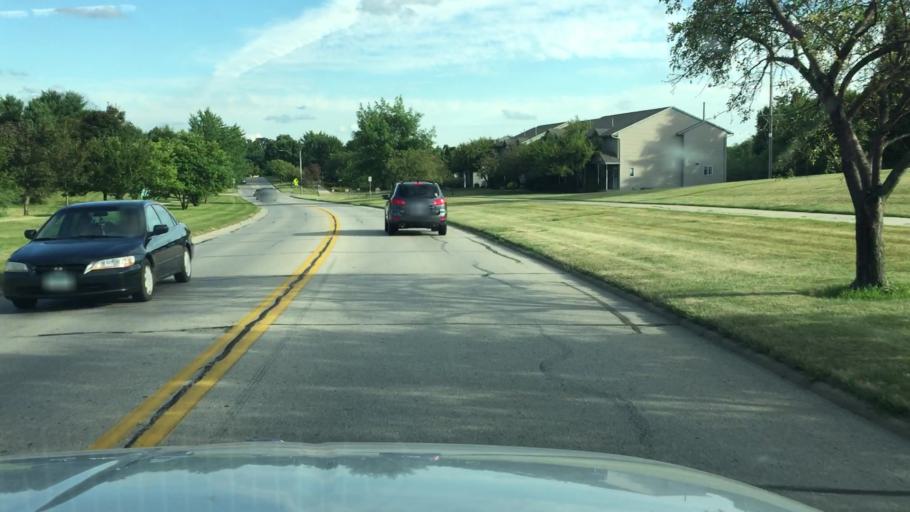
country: US
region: Iowa
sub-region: Johnson County
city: Iowa City
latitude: 41.6619
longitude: -91.4828
